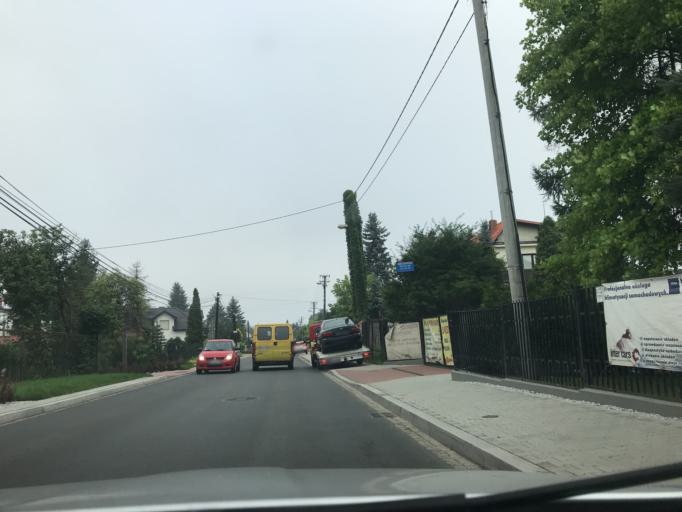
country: PL
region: Lesser Poland Voivodeship
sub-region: Powiat krakowski
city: Ochojno
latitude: 50.0063
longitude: 19.9806
